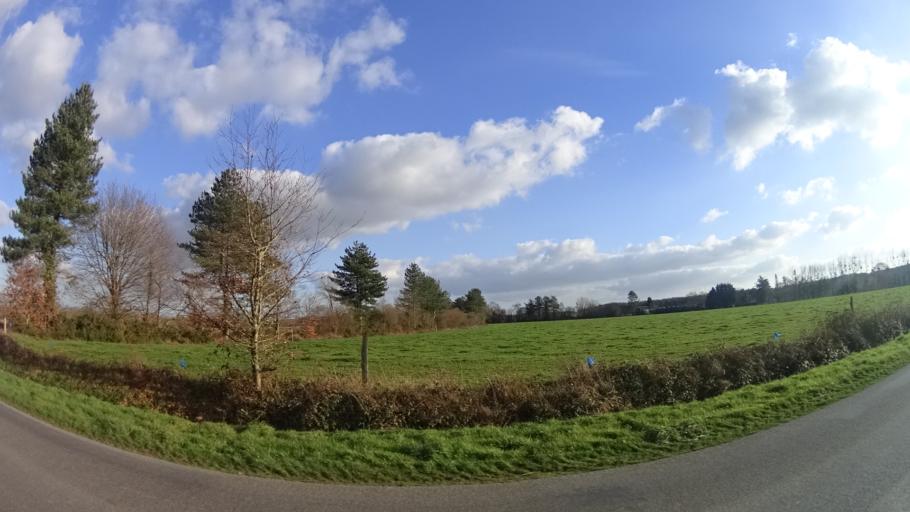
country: FR
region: Pays de la Loire
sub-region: Departement de la Loire-Atlantique
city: Guemene-Penfao
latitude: 47.5915
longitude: -1.8523
